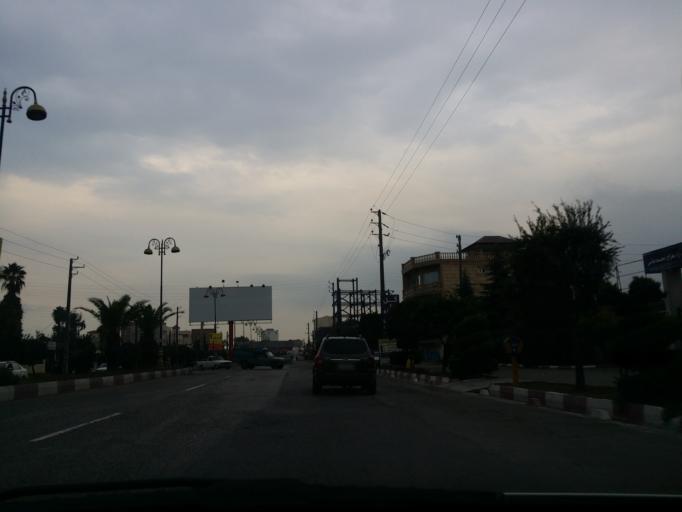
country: IR
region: Mazandaran
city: `Abbasabad
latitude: 36.7267
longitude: 51.1148
